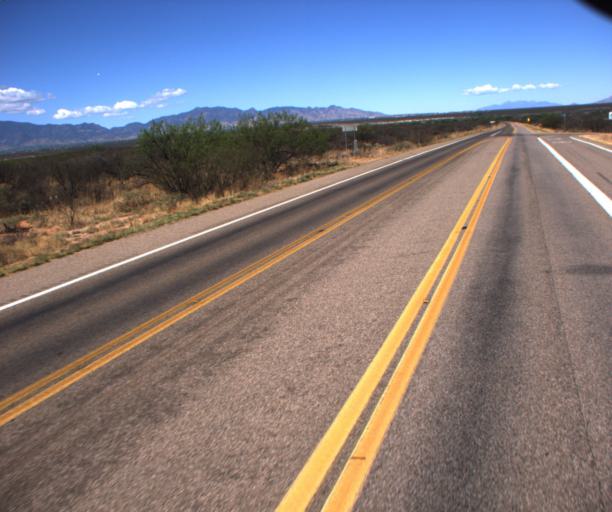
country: US
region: Arizona
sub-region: Cochise County
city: Sierra Vista Southeast
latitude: 31.5513
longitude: -110.1159
